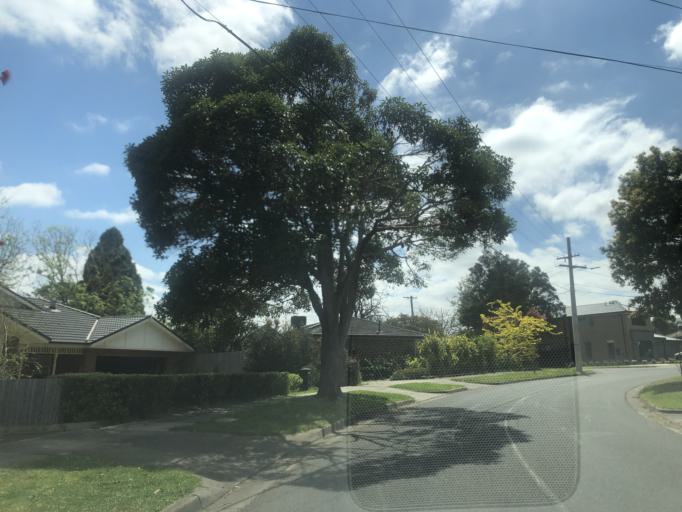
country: AU
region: Victoria
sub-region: Monash
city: Notting Hill
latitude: -37.9222
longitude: 145.1633
